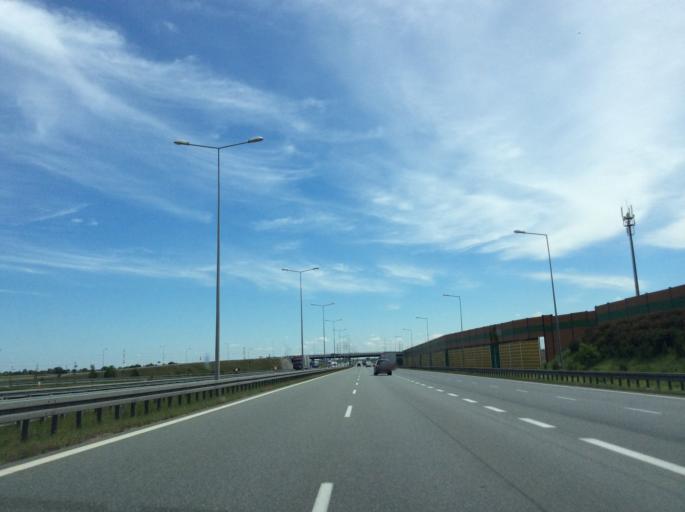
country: PL
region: Greater Poland Voivodeship
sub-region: Powiat poznanski
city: Komorniki
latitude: 52.3504
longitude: 16.7704
